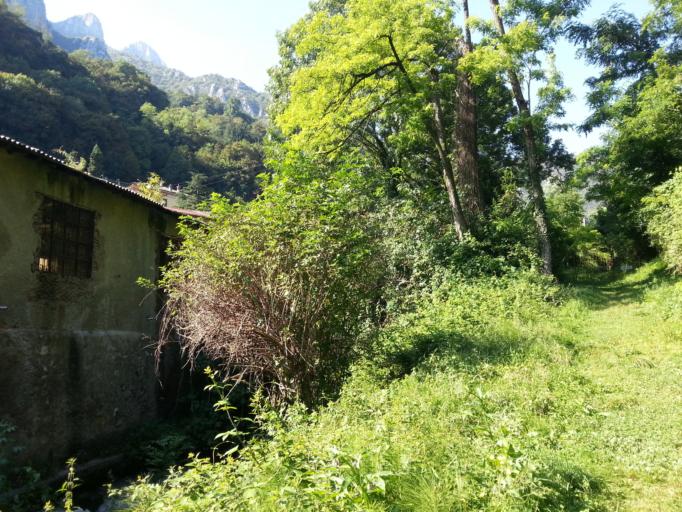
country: IT
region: Lombardy
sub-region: Provincia di Lecco
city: Ballabio
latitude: 45.8758
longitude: 9.4052
